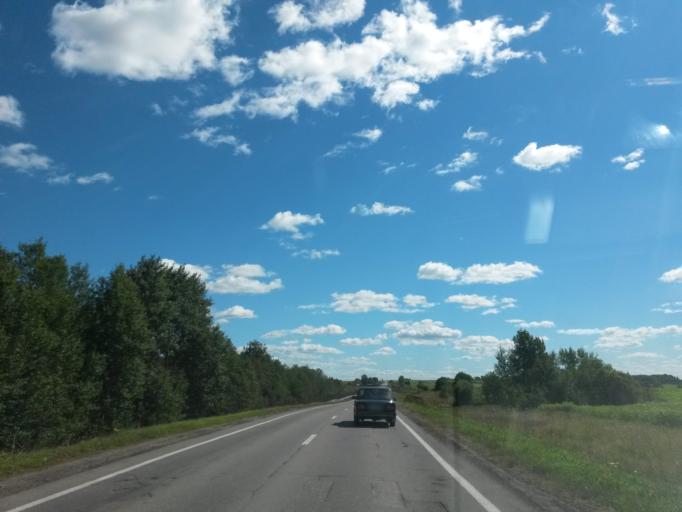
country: RU
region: Jaroslavl
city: Yaroslavl
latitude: 57.7812
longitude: 39.8441
